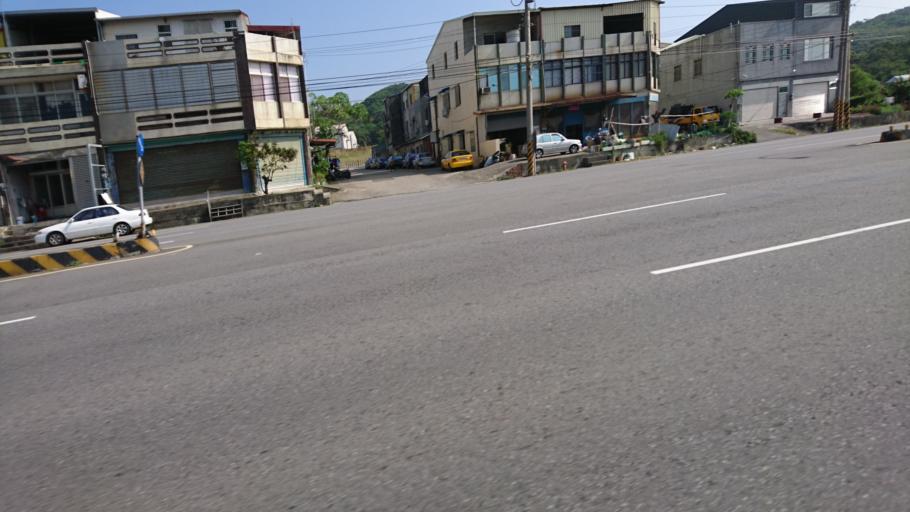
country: TW
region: Taiwan
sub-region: Miaoli
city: Miaoli
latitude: 24.5142
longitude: 120.6909
